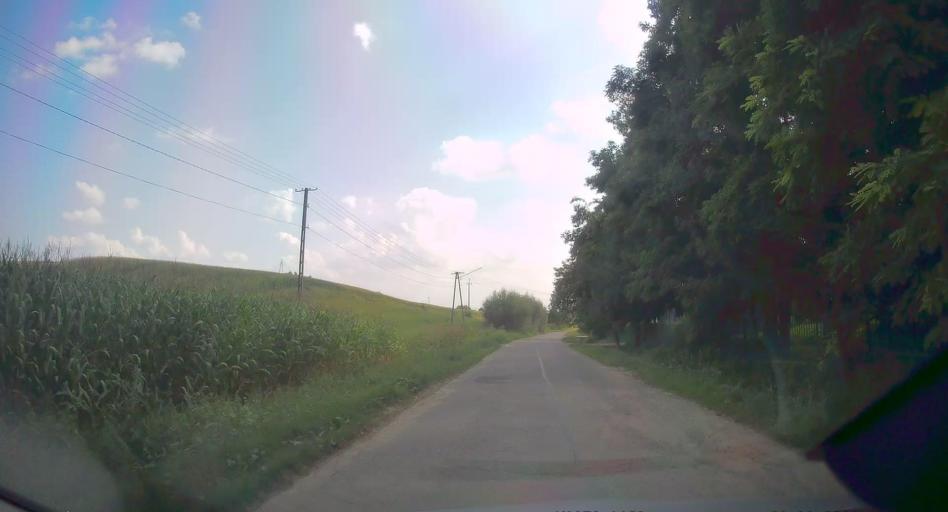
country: PL
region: Lesser Poland Voivodeship
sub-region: Powiat bochenski
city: Dziewin
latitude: 50.1490
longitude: 20.4646
